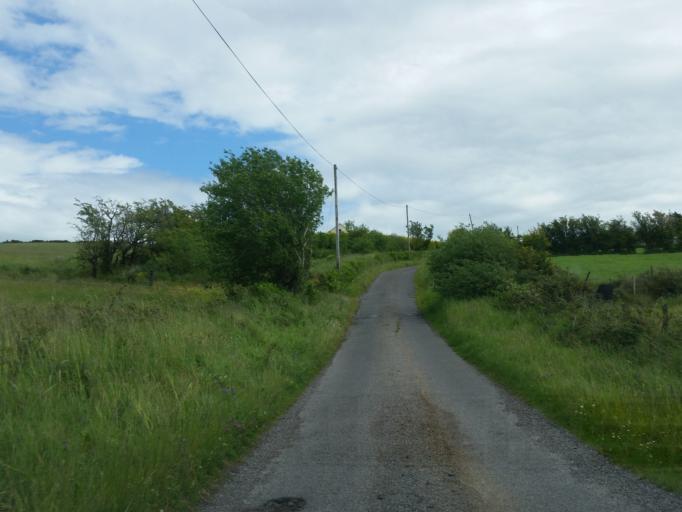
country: GB
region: Northern Ireland
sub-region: Omagh District
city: Omagh
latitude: 54.5579
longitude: -7.0628
